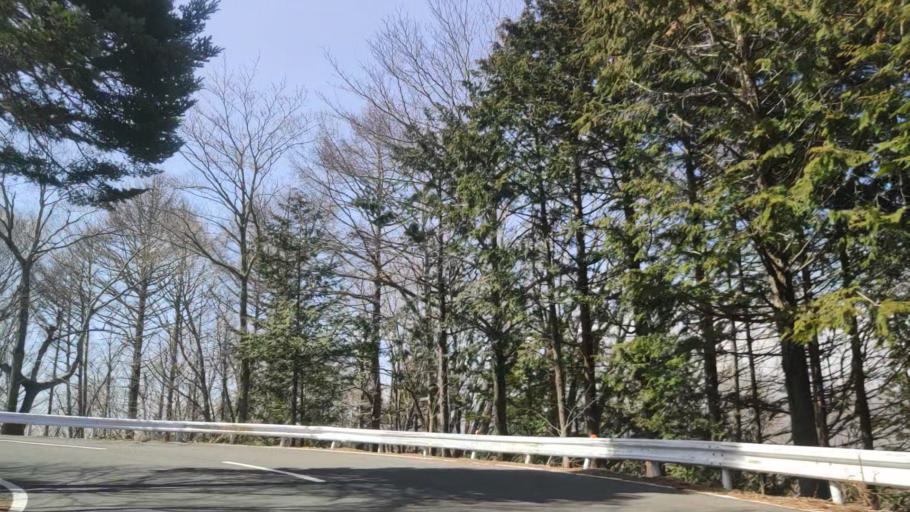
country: JP
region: Yamanashi
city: Fujikawaguchiko
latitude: 35.4603
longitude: 138.8178
